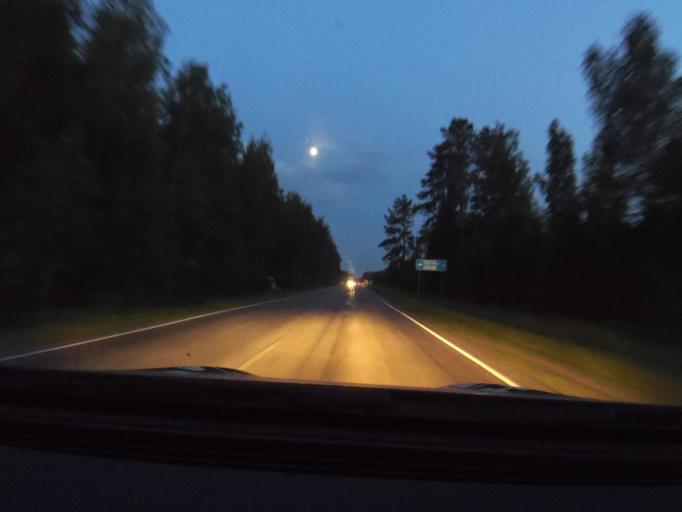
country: RU
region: Bashkortostan
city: Duvan
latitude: 56.0081
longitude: 58.2130
